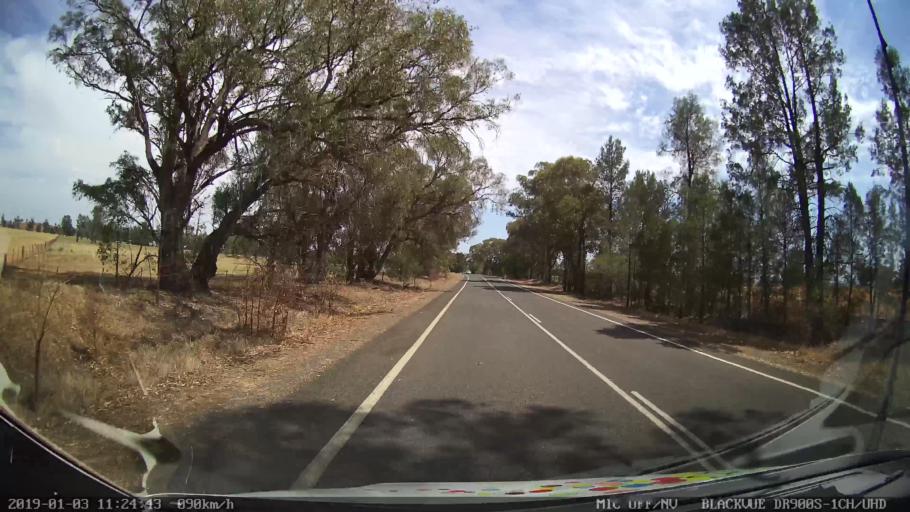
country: AU
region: New South Wales
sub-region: Weddin
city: Grenfell
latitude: -34.0478
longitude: 148.2332
